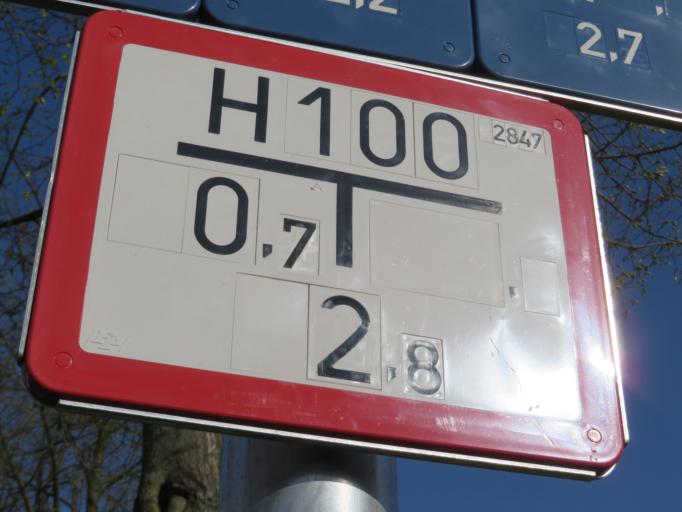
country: DE
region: North Rhine-Westphalia
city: Witten
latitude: 51.4374
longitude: 7.3656
